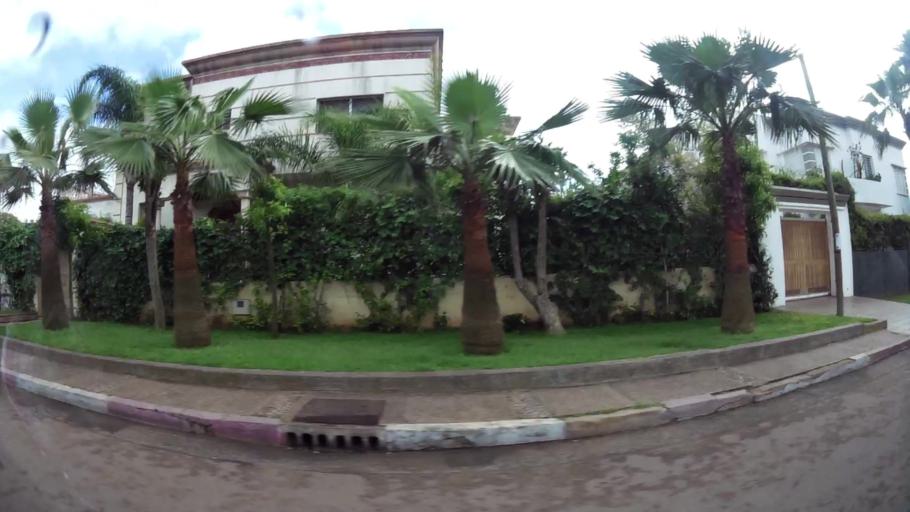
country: MA
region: Grand Casablanca
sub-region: Casablanca
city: Casablanca
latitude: 33.5405
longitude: -7.6353
